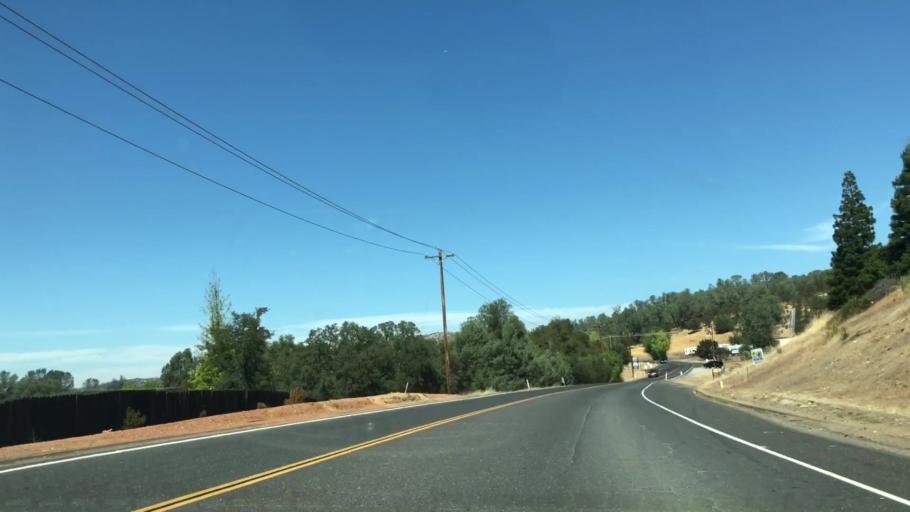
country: US
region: California
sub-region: Calaveras County
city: Copperopolis
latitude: 37.9377
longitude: -120.6051
